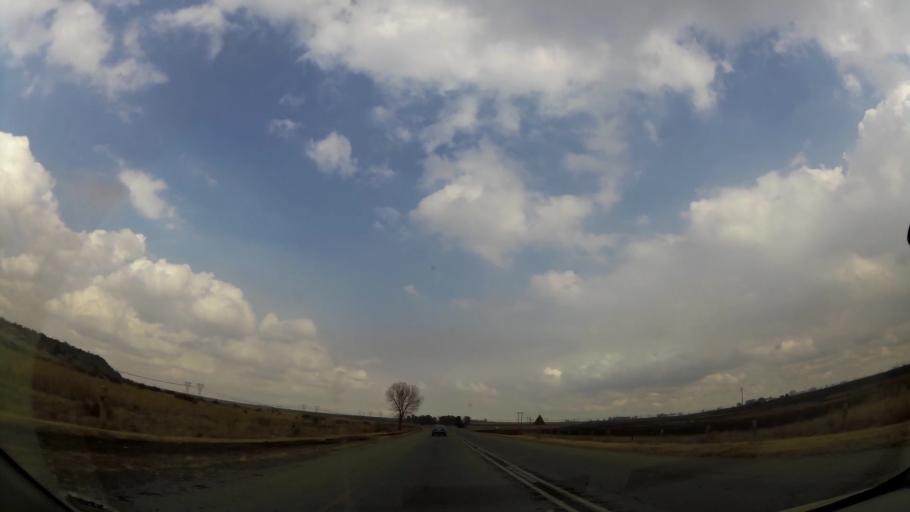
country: ZA
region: Orange Free State
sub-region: Fezile Dabi District Municipality
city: Sasolburg
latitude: -26.8052
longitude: 27.9129
